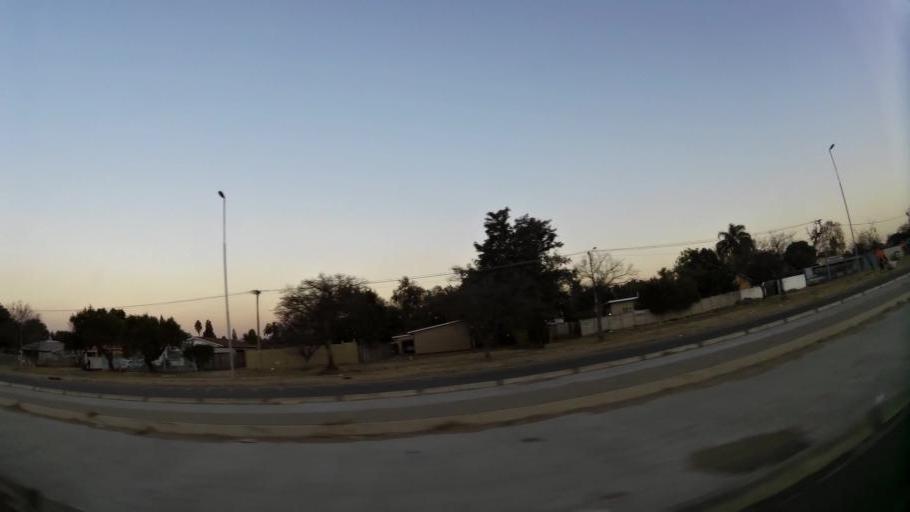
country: ZA
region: North-West
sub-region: Bojanala Platinum District Municipality
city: Rustenburg
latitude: -25.6495
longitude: 27.2524
